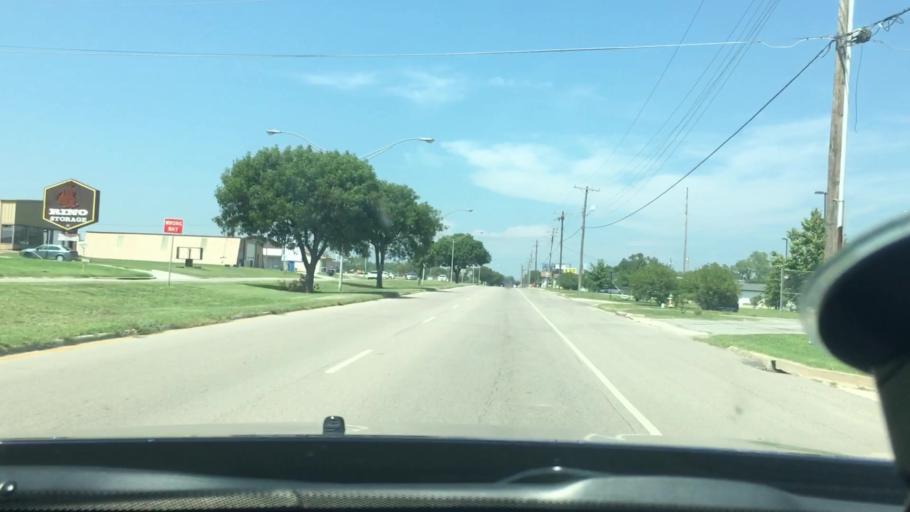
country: US
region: Oklahoma
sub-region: Pontotoc County
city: Ada
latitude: 34.7925
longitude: -96.6786
